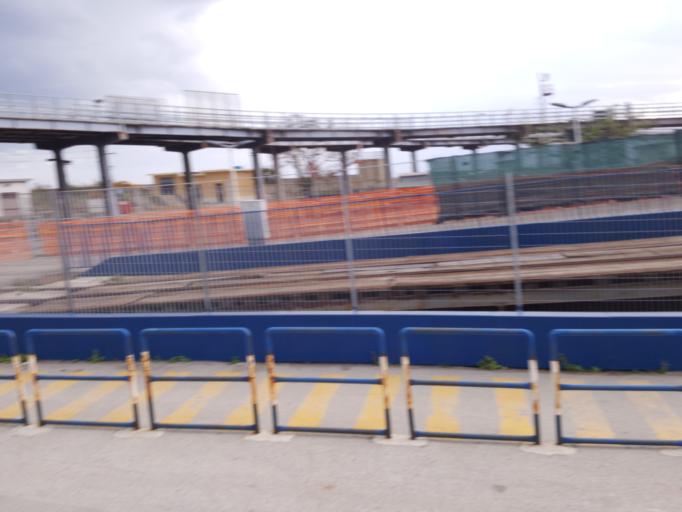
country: IT
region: Calabria
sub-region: Provincia di Reggio Calabria
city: Campo Calabro
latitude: 38.2163
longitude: 15.6342
